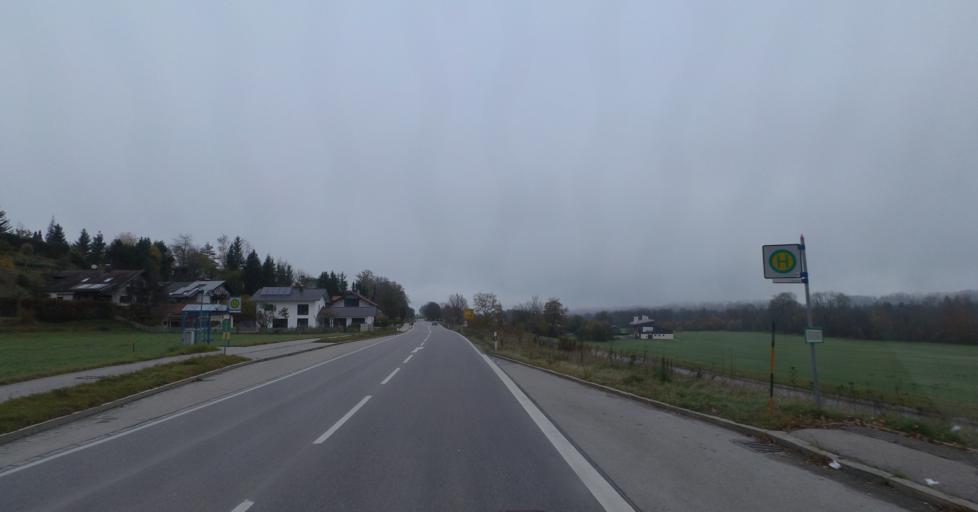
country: DE
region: Bavaria
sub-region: Upper Bavaria
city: Trostberg an der Alz
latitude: 48.0444
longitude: 12.5634
